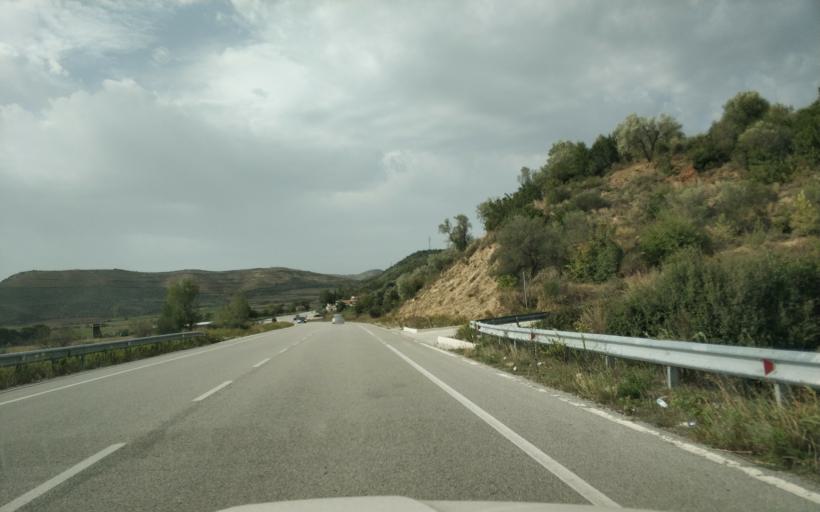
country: AL
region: Gjirokaster
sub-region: Rrethi i Tepelenes
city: Krahes
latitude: 40.3863
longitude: 19.8847
